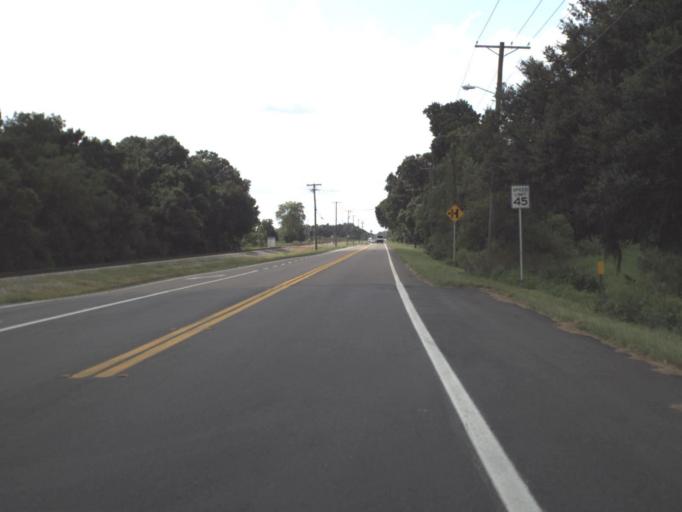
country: US
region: Florida
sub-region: Hillsborough County
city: Plant City
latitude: 28.0621
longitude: -82.1341
